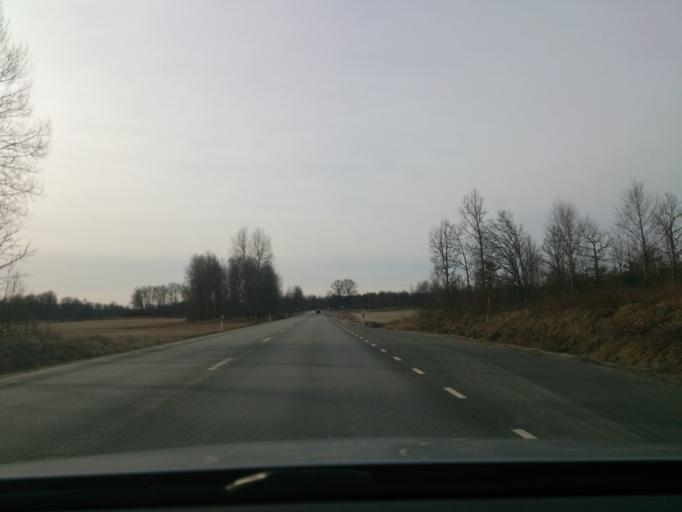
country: SE
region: Kronoberg
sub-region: Alvesta Kommun
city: Alvesta
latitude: 56.9387
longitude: 14.5598
